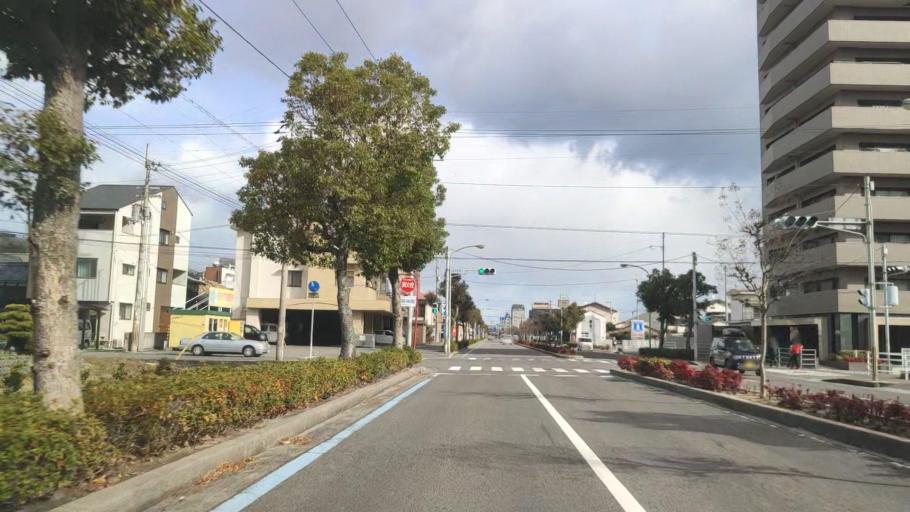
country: JP
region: Ehime
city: Hojo
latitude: 34.0610
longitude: 132.9846
